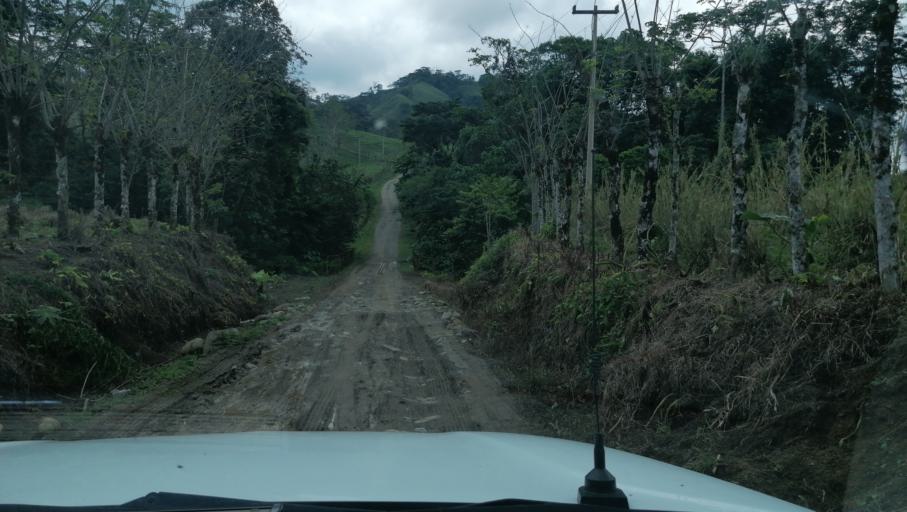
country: MX
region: Chiapas
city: Pichucalco
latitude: 17.4557
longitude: -93.2038
